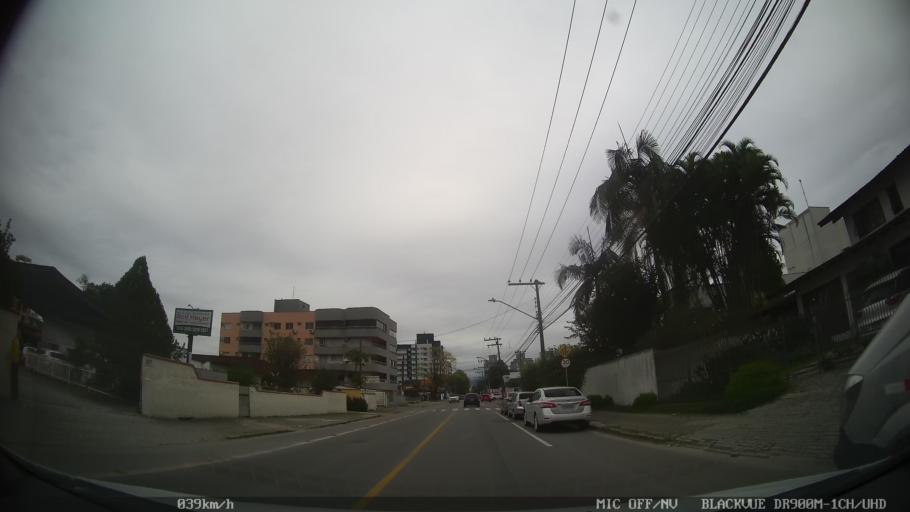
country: BR
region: Santa Catarina
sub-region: Joinville
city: Joinville
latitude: -26.2747
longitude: -48.8535
